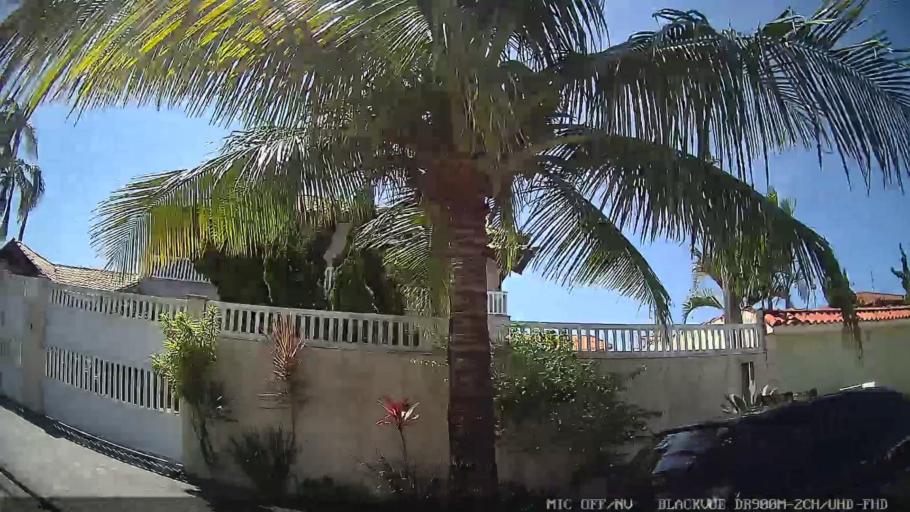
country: BR
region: Sao Paulo
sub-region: Peruibe
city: Peruibe
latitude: -24.3047
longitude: -46.9748
